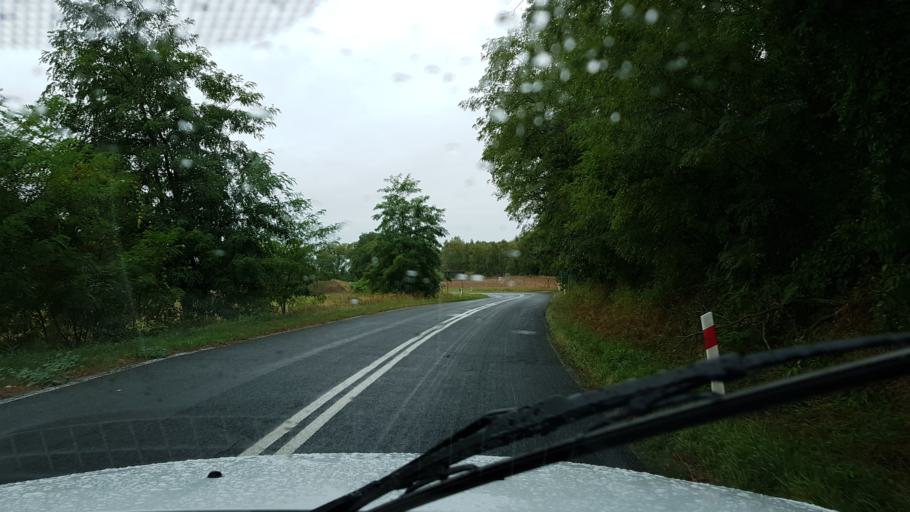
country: PL
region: West Pomeranian Voivodeship
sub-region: Powiat gryfinski
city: Cedynia
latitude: 52.8321
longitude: 14.1776
